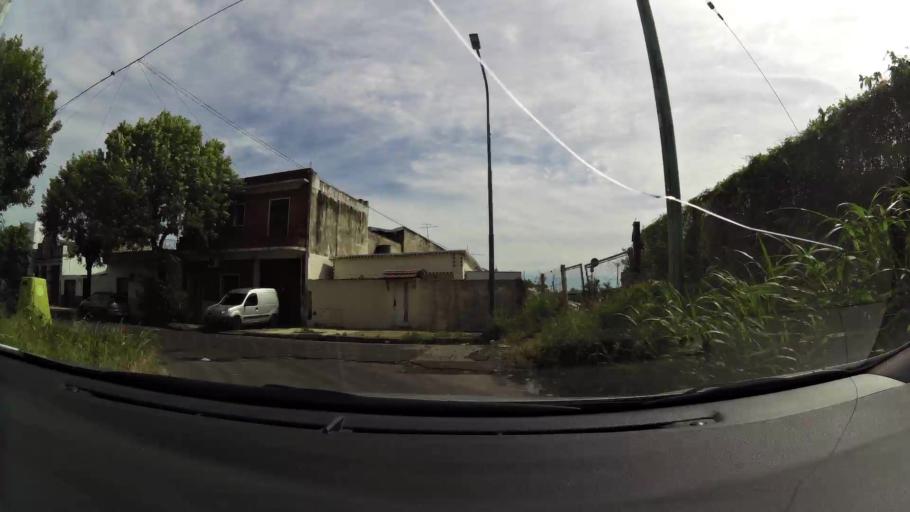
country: AR
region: Buenos Aires F.D.
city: Villa Lugano
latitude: -34.6589
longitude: -58.4331
